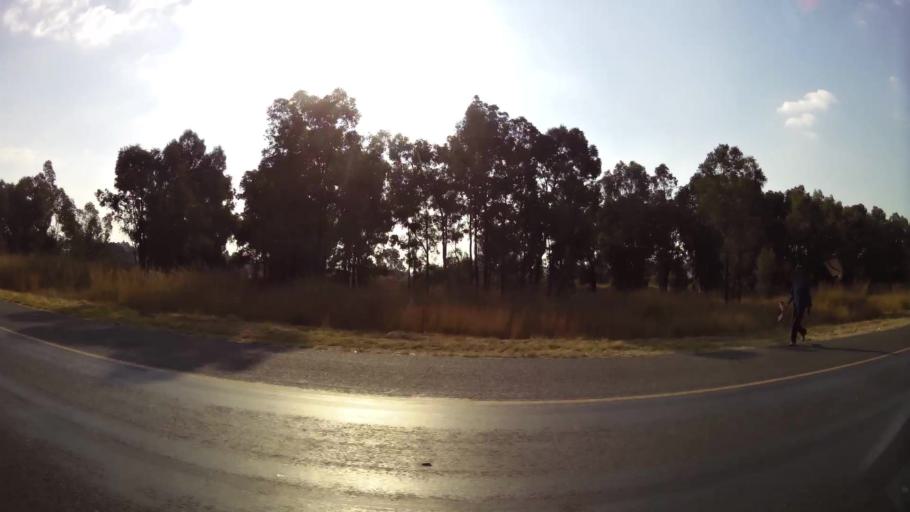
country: ZA
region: Gauteng
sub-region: City of Johannesburg Metropolitan Municipality
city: Modderfontein
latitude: -26.1086
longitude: 28.1643
